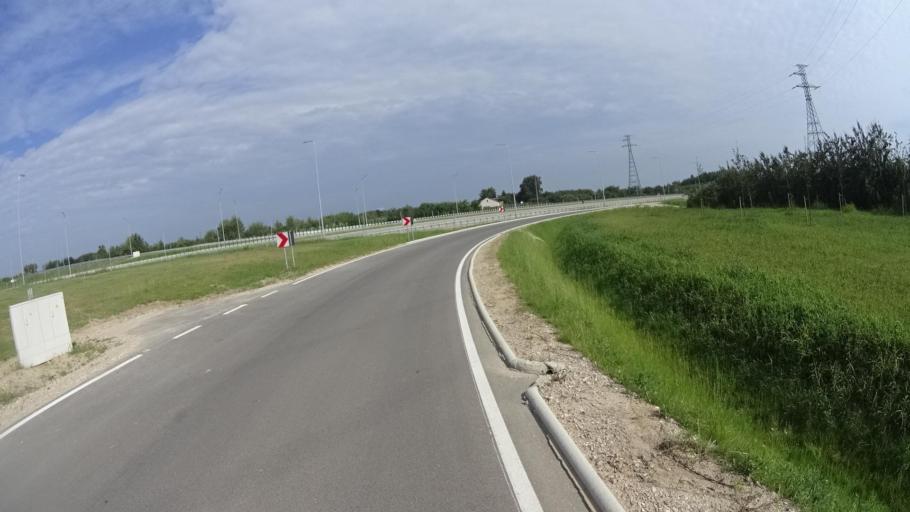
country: PL
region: Masovian Voivodeship
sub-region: Powiat piaseczynski
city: Tarczyn
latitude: 51.9517
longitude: 20.8469
